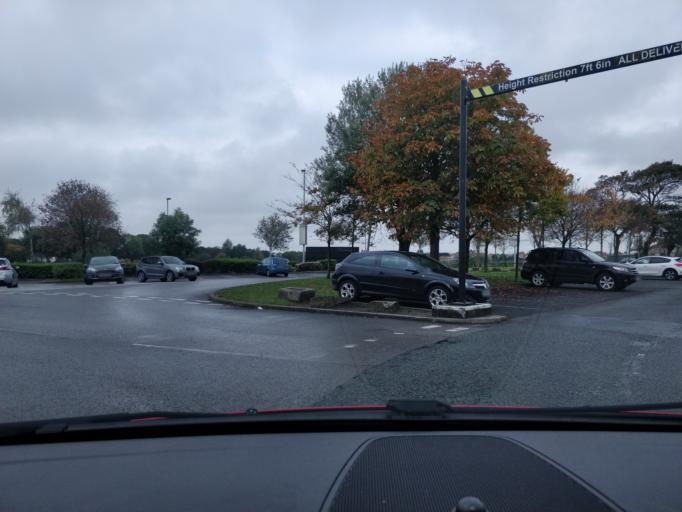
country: GB
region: England
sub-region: Sefton
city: Southport
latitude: 53.6345
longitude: -2.9694
